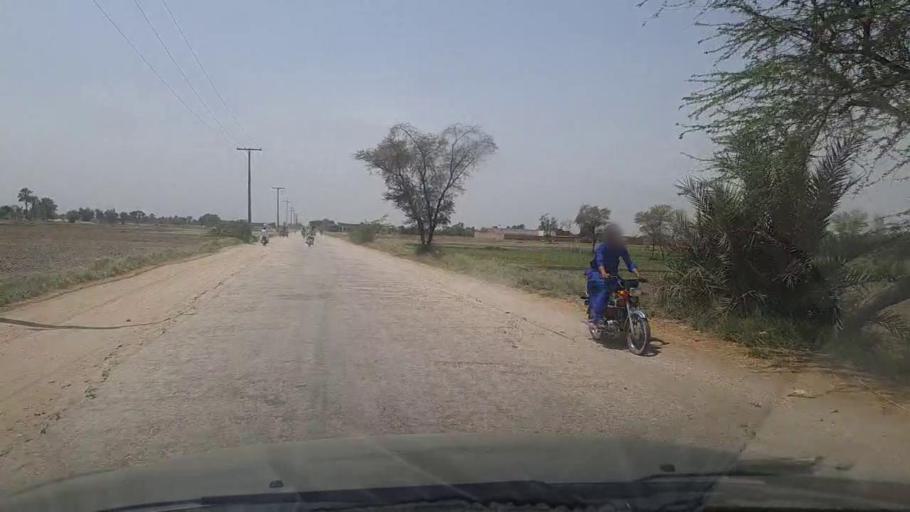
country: PK
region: Sindh
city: Bhiria
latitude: 26.8923
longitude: 68.2517
